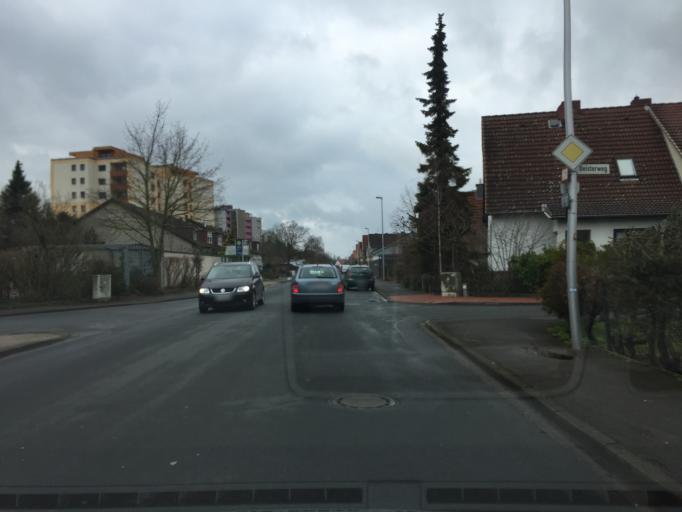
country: DE
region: Lower Saxony
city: Wunstorf
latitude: 52.4159
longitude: 9.4394
